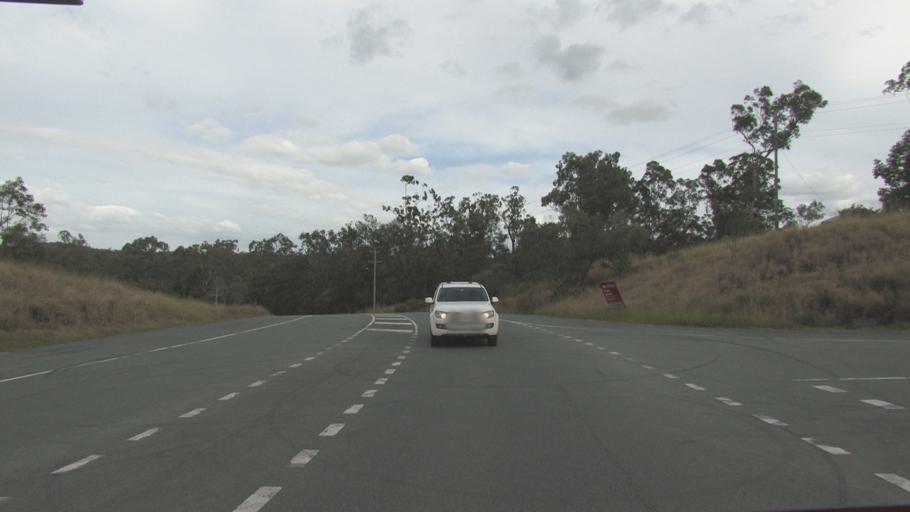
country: AU
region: Queensland
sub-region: Logan
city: Beenleigh
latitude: -27.7128
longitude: 153.1702
